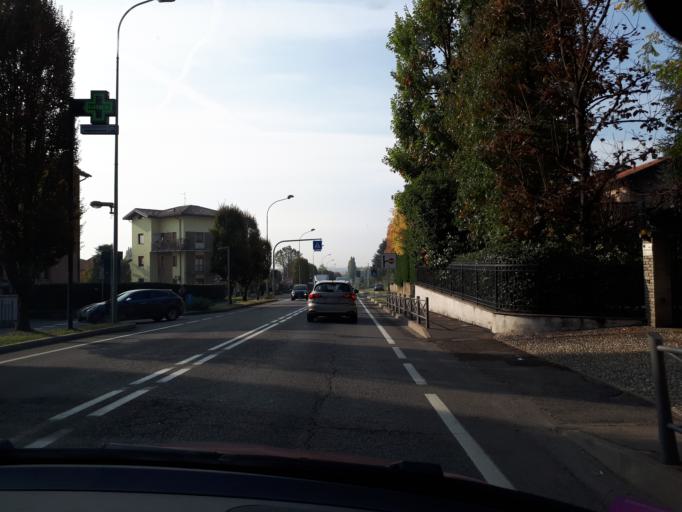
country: IT
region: Lombardy
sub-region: Provincia di Monza e Brianza
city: Lesmo
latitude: 45.6470
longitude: 9.3075
